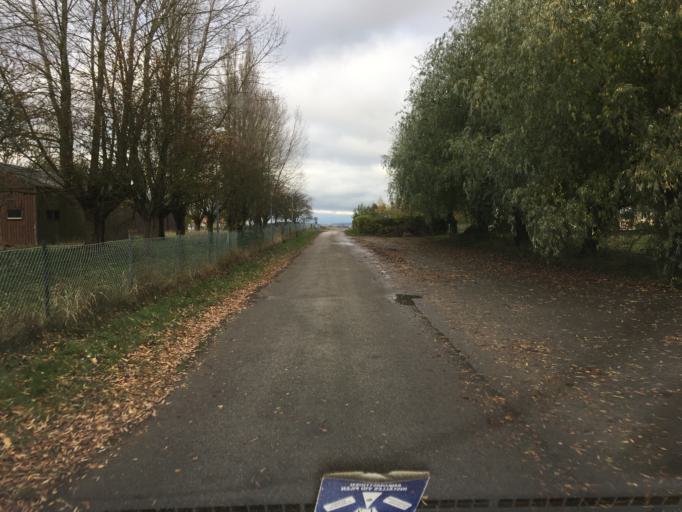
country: SE
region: Skane
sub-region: Lunds Kommun
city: Lund
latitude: 55.7488
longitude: 13.2086
